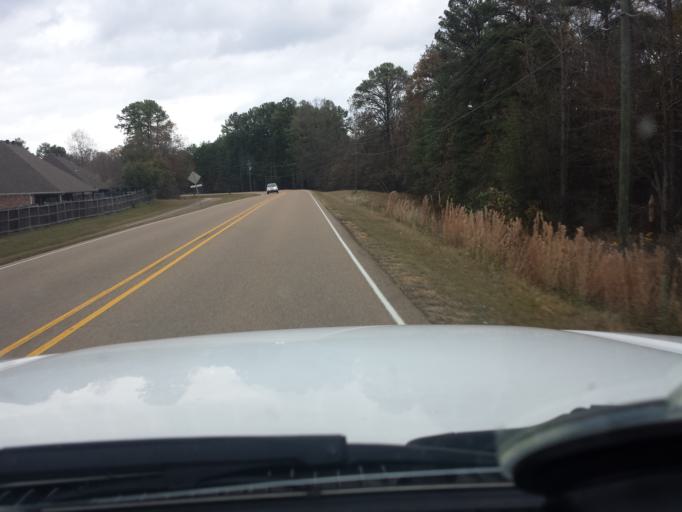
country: US
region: Mississippi
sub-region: Madison County
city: Madison
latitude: 32.4107
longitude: -90.0088
